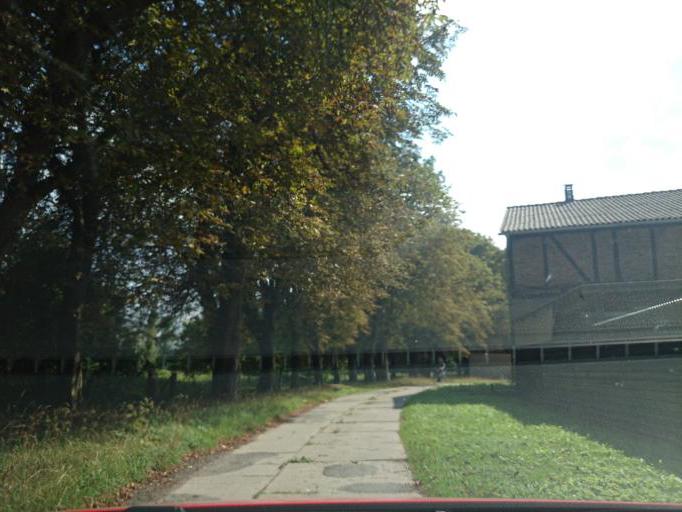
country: DE
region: Mecklenburg-Vorpommern
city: Barth
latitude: 54.3671
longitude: 12.7356
